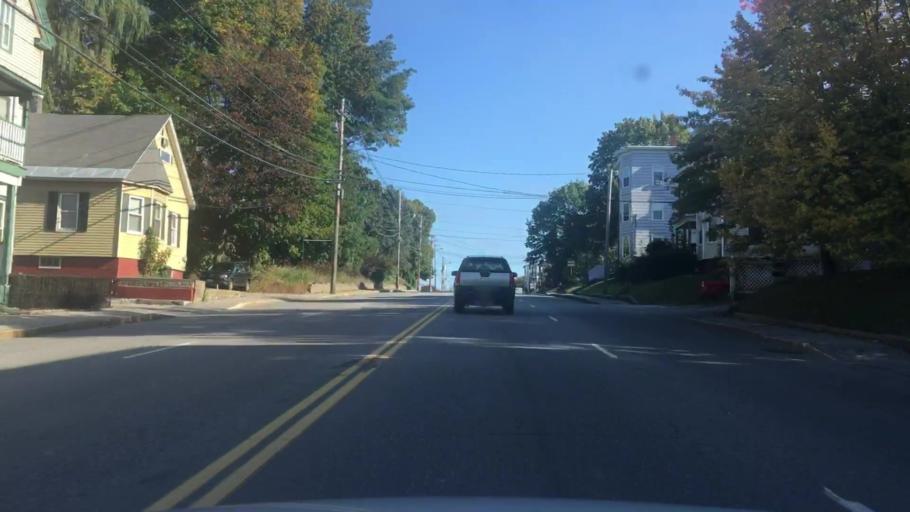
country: US
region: Maine
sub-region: Androscoggin County
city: Lewiston
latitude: 44.0870
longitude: -70.2087
